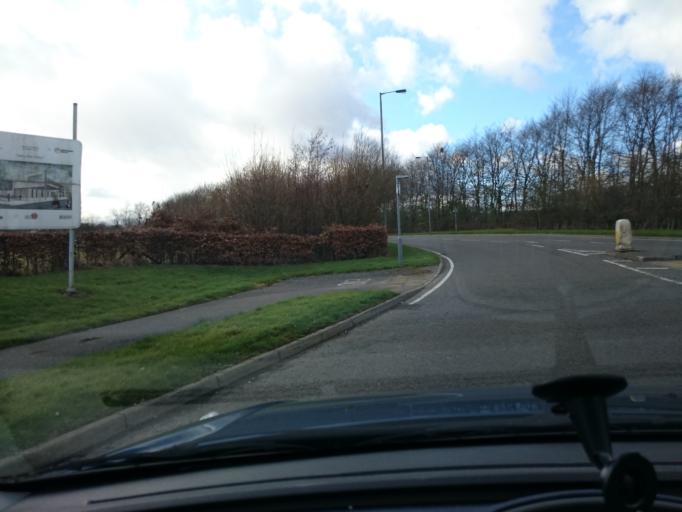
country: GB
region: Scotland
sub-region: Falkirk
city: Denny
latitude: 56.0222
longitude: -3.8958
